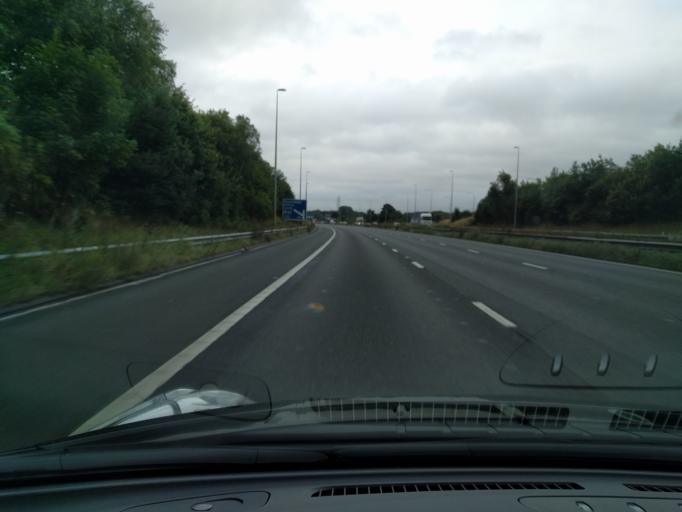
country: GB
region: England
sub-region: Warrington
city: Winwick
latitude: 53.4397
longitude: -2.5833
